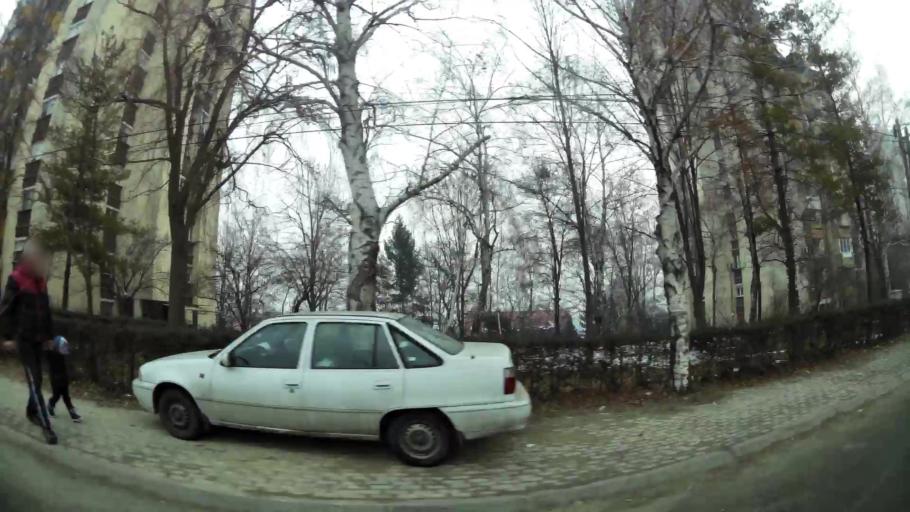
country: MK
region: Cair
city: Cair
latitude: 42.0106
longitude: 21.4599
